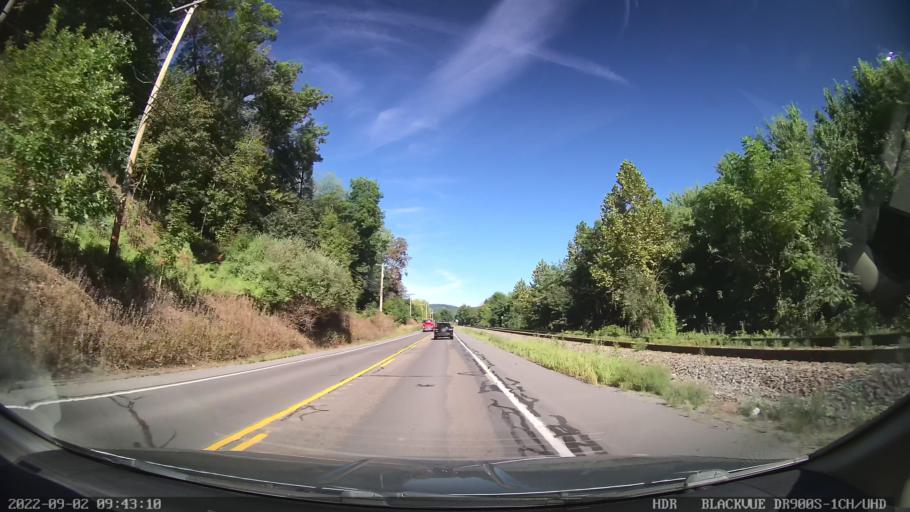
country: US
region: Pennsylvania
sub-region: Montour County
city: Danville
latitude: 40.9515
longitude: -76.6168
